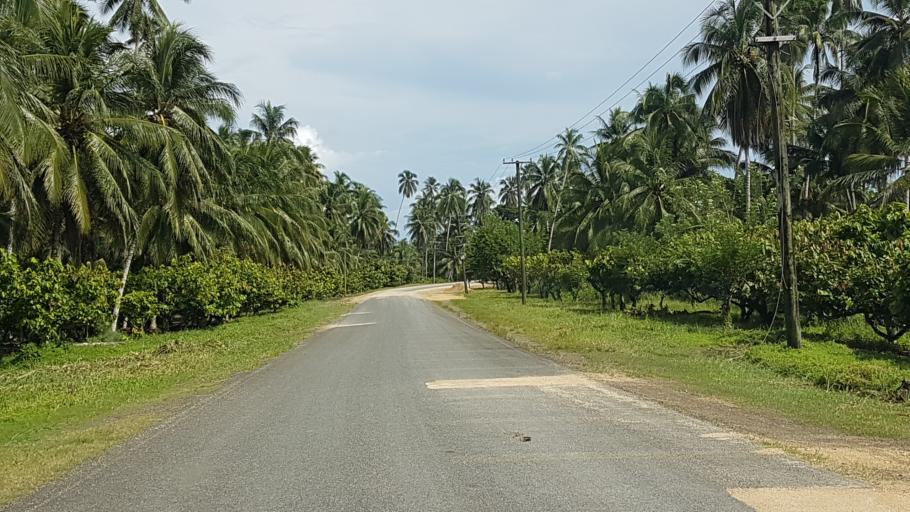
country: PG
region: Madang
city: Madang
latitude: -4.9794
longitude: 145.7761
